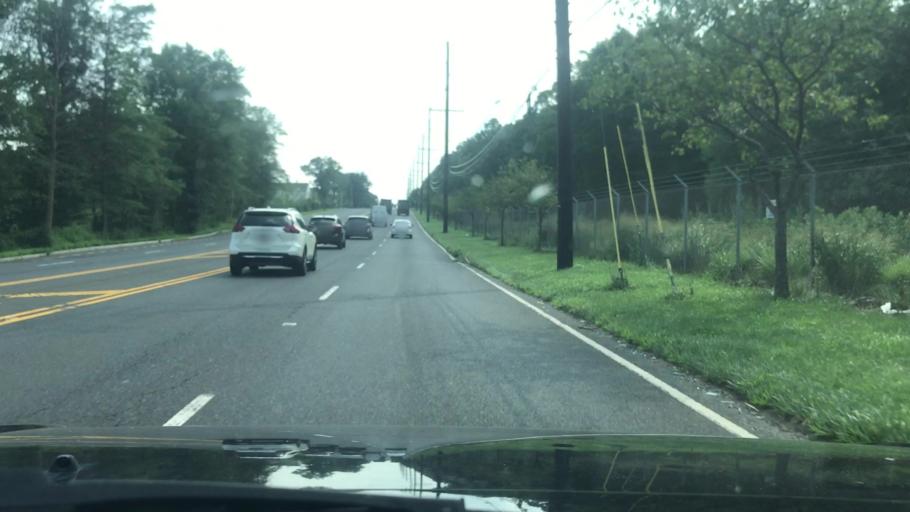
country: US
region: New Jersey
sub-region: Monmouth County
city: Tinton Falls
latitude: 40.2643
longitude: -74.0870
